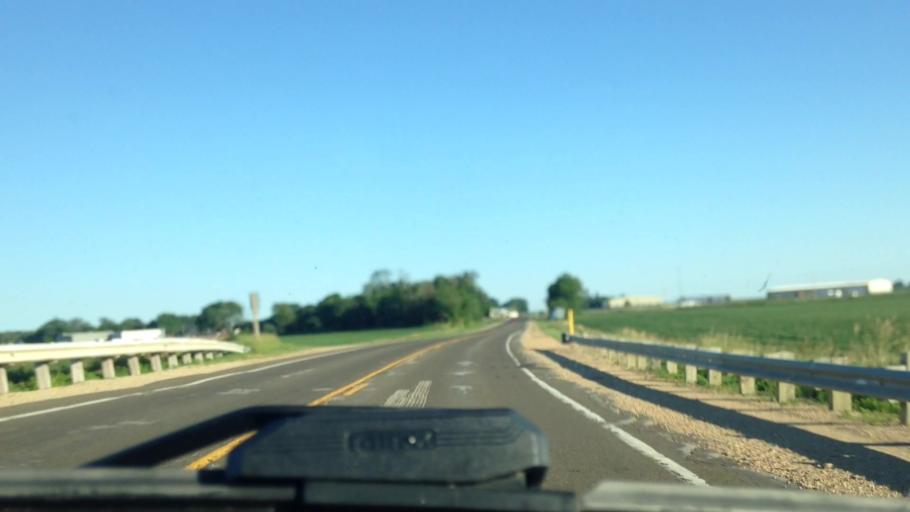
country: US
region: Wisconsin
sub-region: Columbia County
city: Poynette
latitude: 43.3341
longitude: -89.3638
